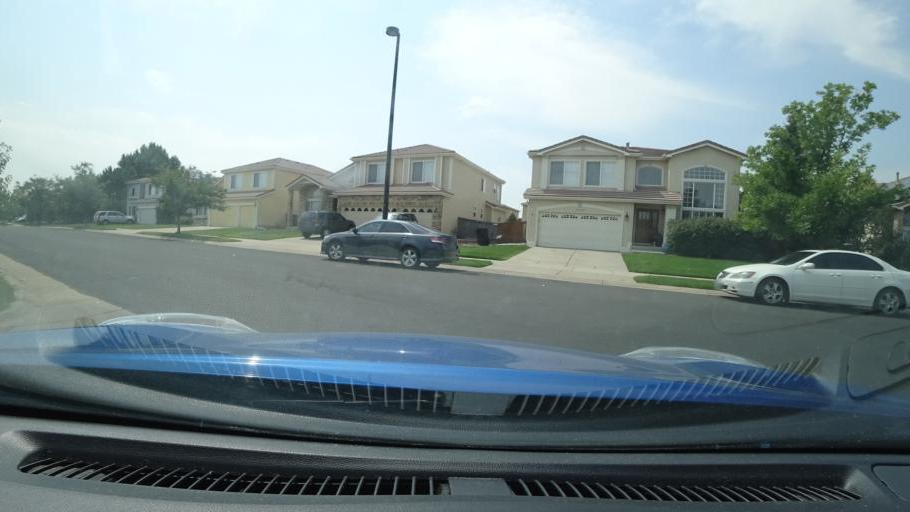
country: US
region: Colorado
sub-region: Adams County
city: Aurora
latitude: 39.7815
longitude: -104.7541
